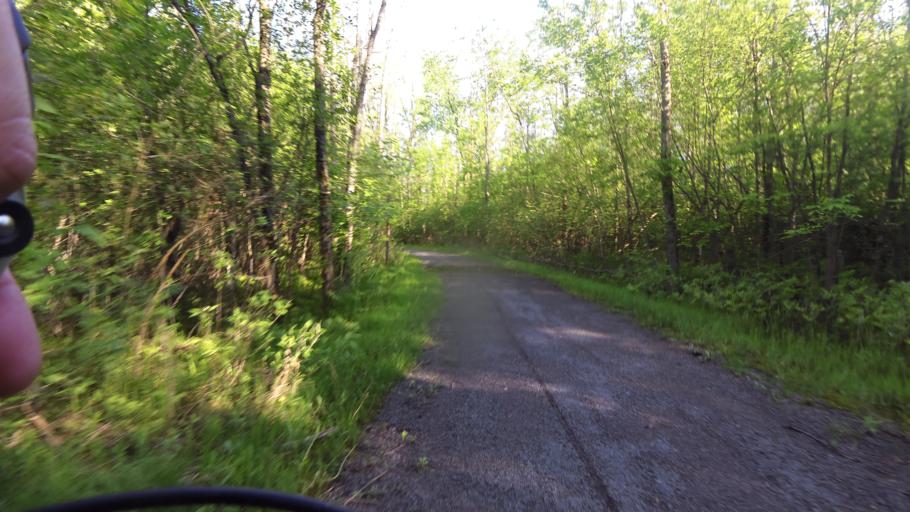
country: CA
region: Ontario
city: Bells Corners
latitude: 45.3618
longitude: -75.8745
